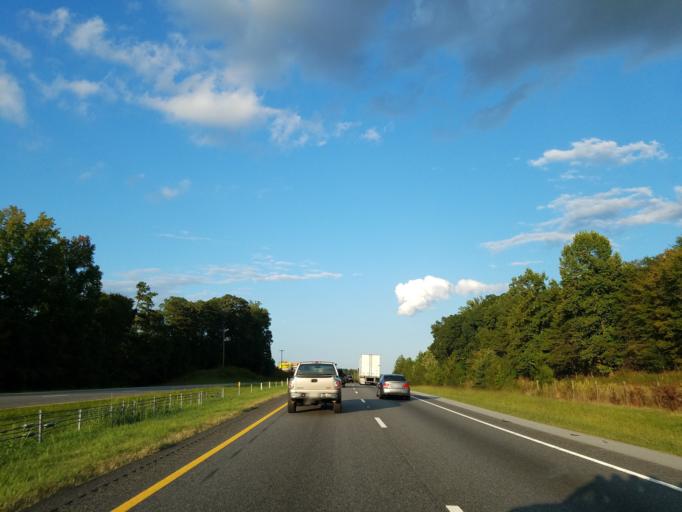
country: US
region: South Carolina
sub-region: Cherokee County
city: Blacksburg
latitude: 35.1225
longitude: -81.5696
